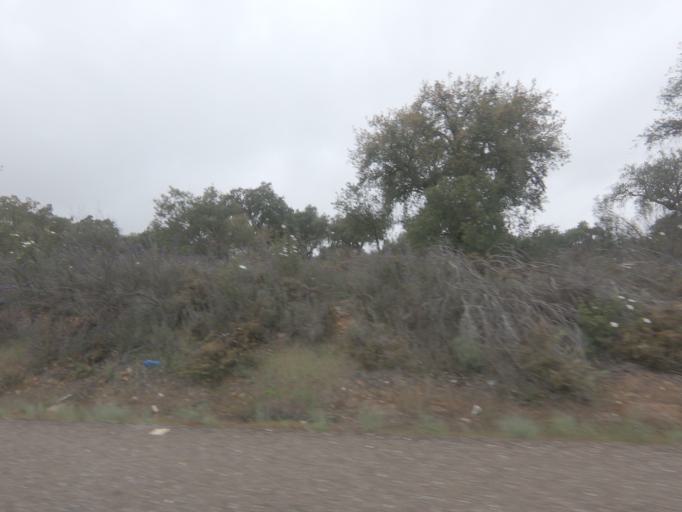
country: ES
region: Extremadura
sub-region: Provincia de Badajoz
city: Puebla de Obando
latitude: 39.1894
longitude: -6.5975
